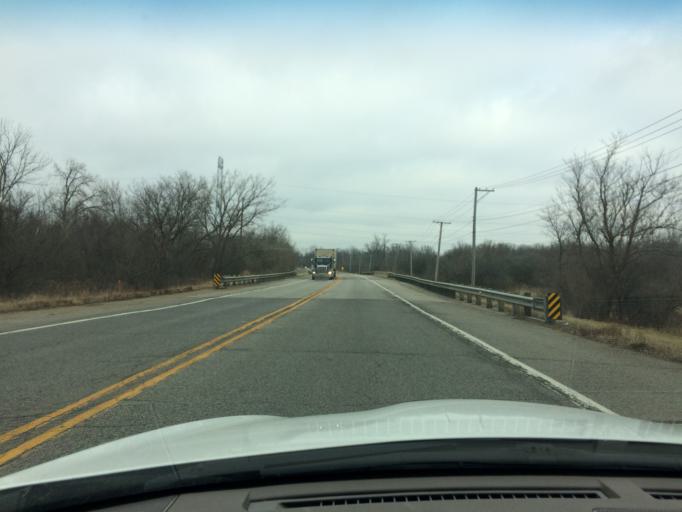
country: US
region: Illinois
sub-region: Kane County
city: Sugar Grove
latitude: 41.8035
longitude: -88.4607
